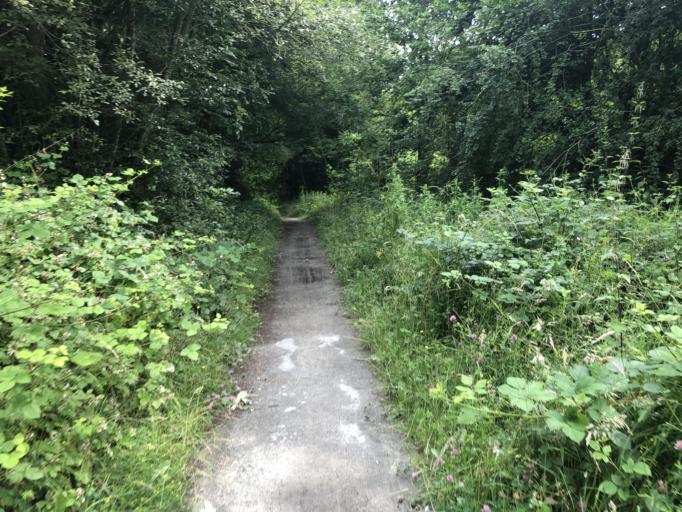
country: GB
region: England
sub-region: Walsall
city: Walsall
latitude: 52.5984
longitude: -1.9739
